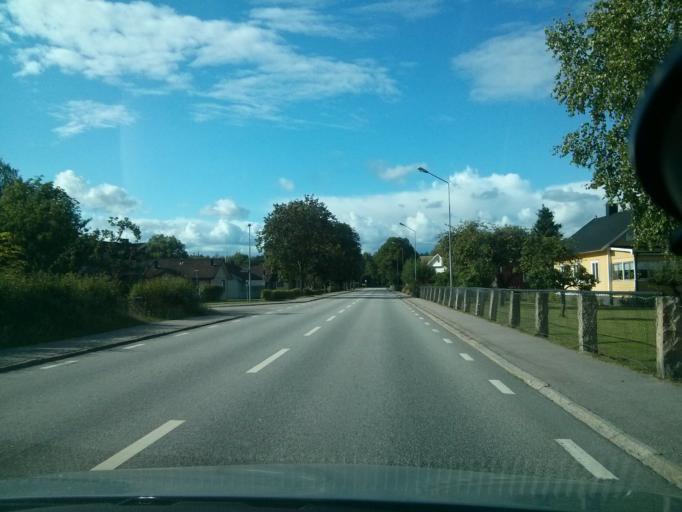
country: SE
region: Blekinge
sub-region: Ronneby Kommun
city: Brakne-Hoby
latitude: 56.3438
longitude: 15.1558
